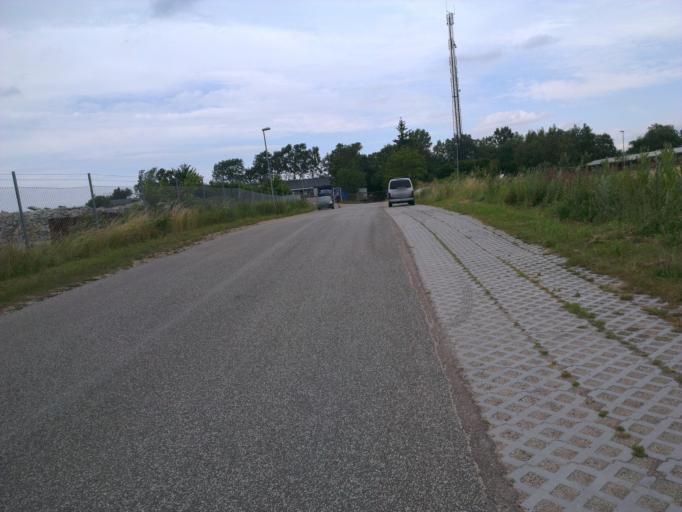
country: DK
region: Capital Region
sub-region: Frederikssund Kommune
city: Skibby
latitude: 55.7614
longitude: 11.9617
